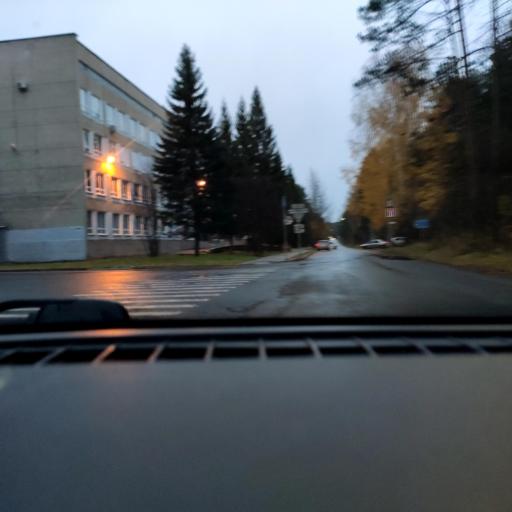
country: RU
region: Perm
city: Perm
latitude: 58.0536
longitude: 56.2305
